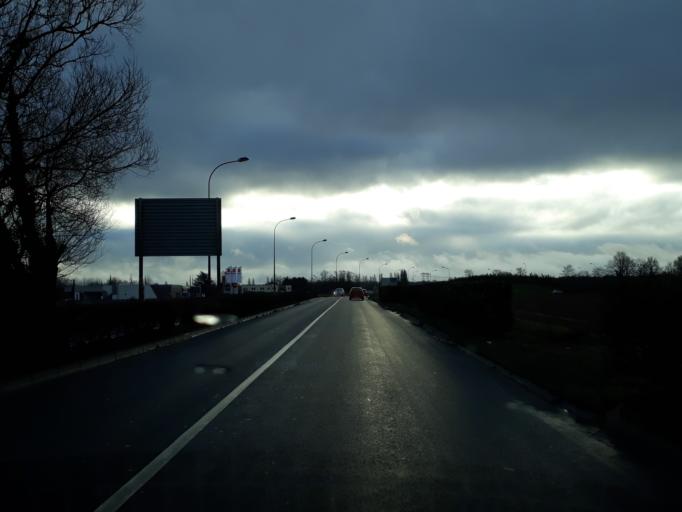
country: FR
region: Ile-de-France
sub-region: Departement de l'Essonne
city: Gometz-le-Chatel
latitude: 48.6750
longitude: 2.1336
